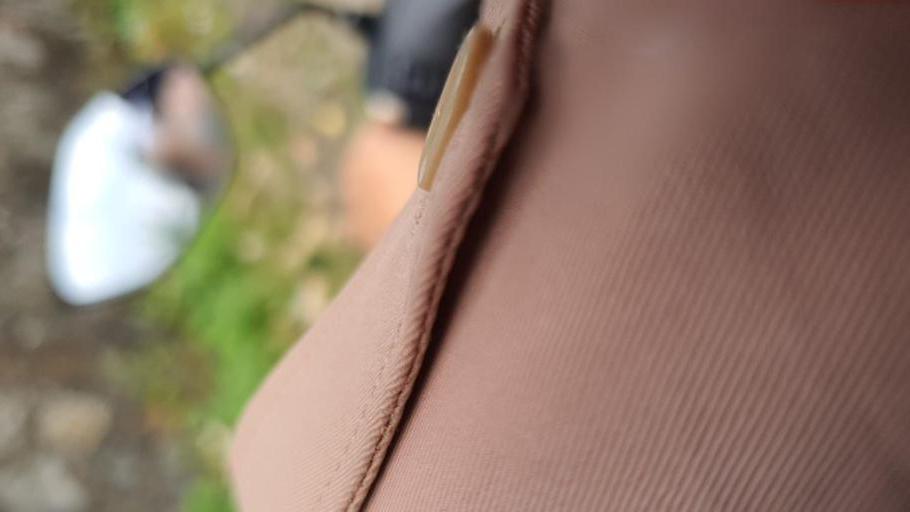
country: ID
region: West Java
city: Caringin
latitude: -6.6449
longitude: 106.8888
